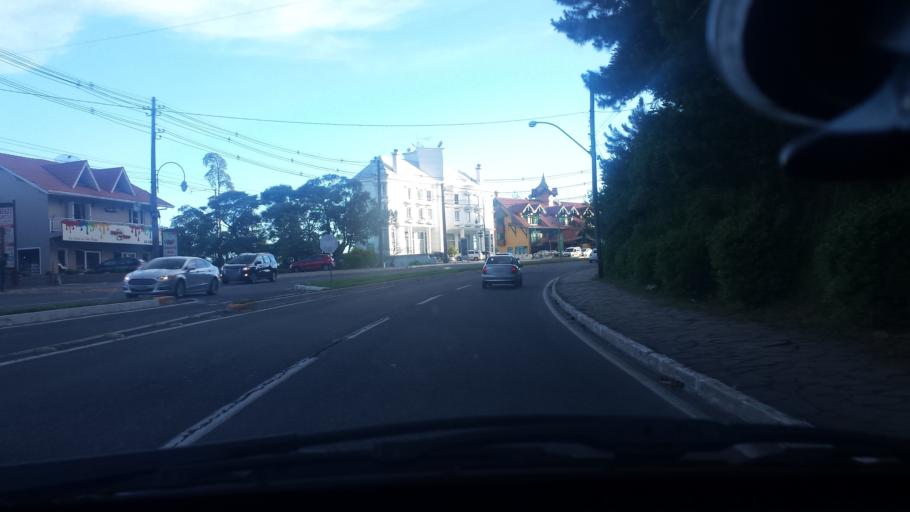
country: BR
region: Rio Grande do Sul
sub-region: Canela
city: Canela
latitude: -29.3765
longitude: -50.8644
